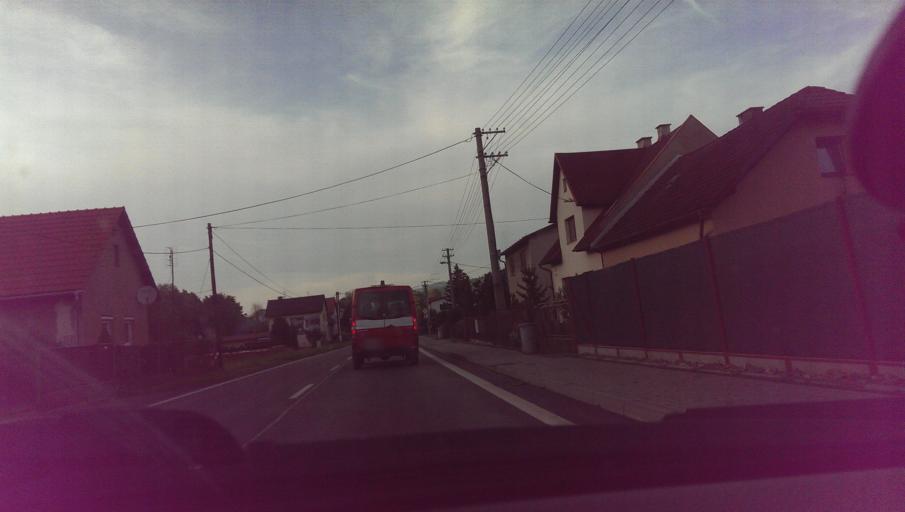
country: CZ
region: Zlin
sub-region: Okres Vsetin
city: Vsetin
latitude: 49.3030
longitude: 18.0022
